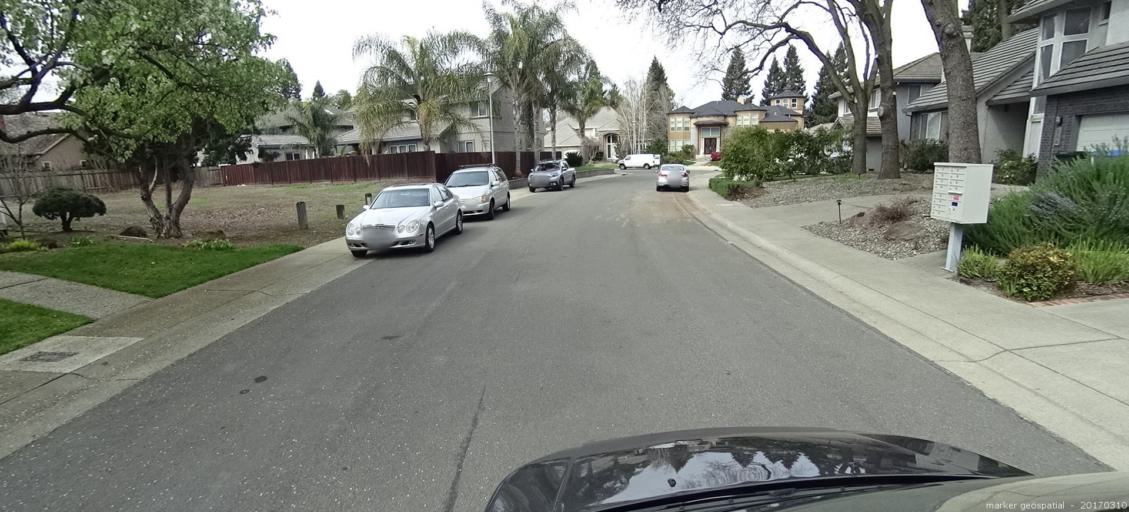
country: US
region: California
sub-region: Sacramento County
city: Parkway
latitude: 38.4779
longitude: -121.5397
